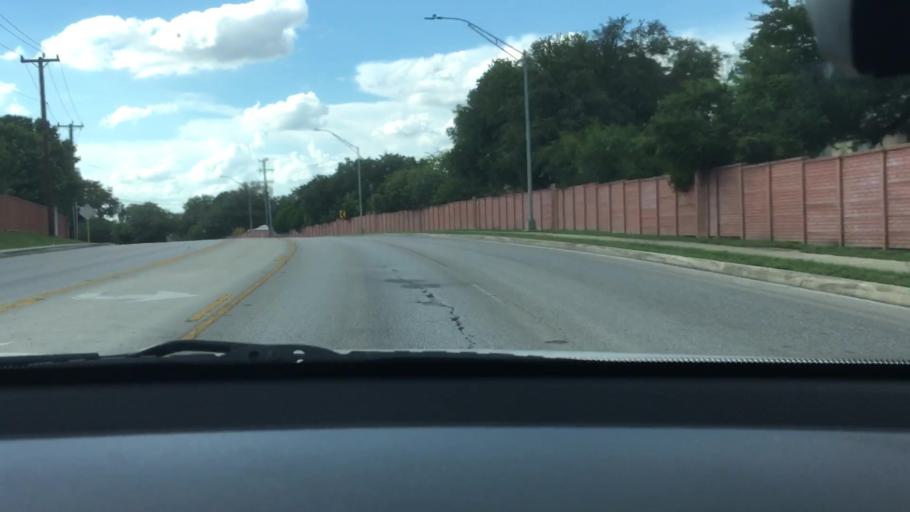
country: US
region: Texas
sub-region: Bexar County
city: Live Oak
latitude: 29.5918
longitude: -98.3975
